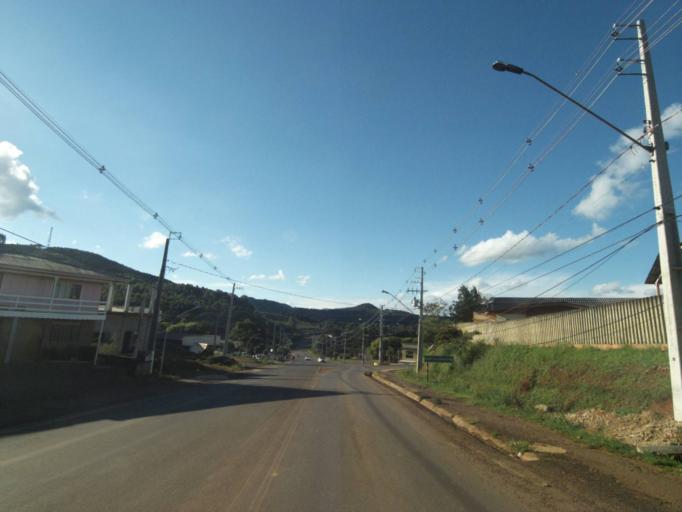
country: BR
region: Parana
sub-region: Uniao Da Vitoria
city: Uniao da Vitoria
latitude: -26.1615
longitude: -51.5380
